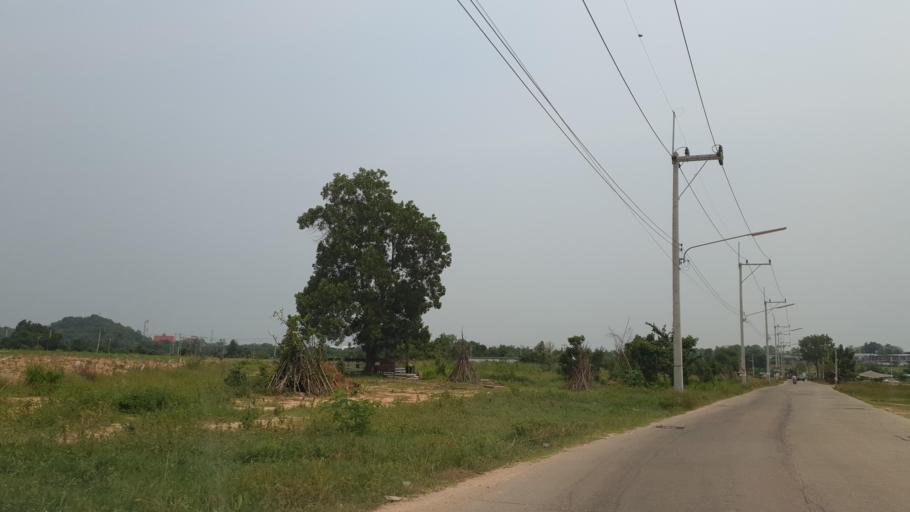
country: TH
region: Chon Buri
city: Phatthaya
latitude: 12.8911
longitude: 100.9270
